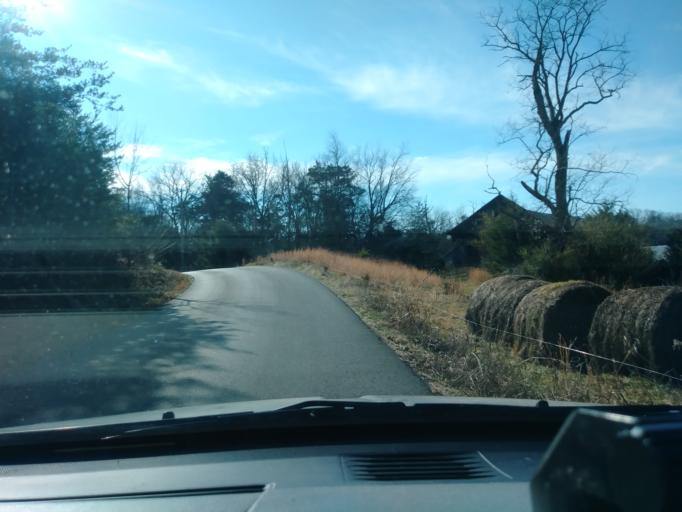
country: US
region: Tennessee
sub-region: Greene County
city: Greeneville
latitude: 36.0801
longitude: -82.8905
